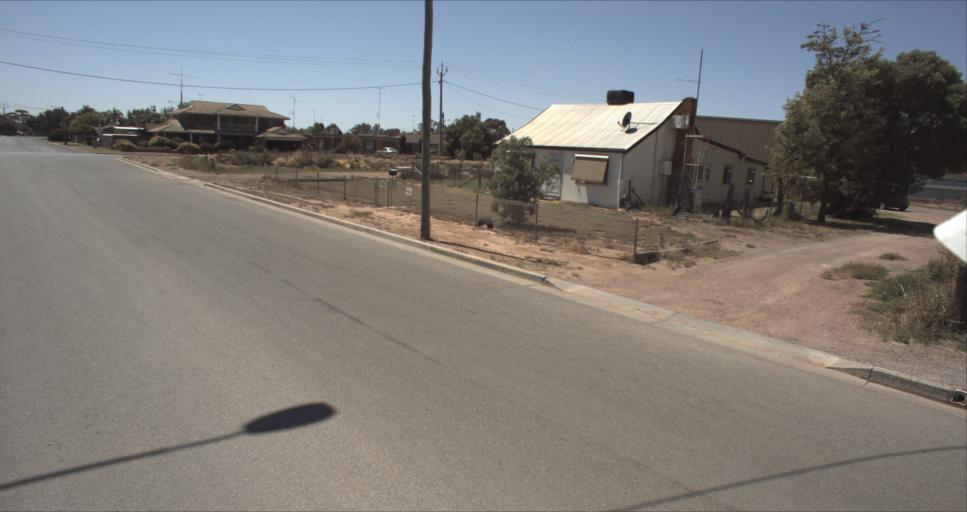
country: AU
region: New South Wales
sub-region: Leeton
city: Leeton
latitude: -34.5474
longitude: 146.3994
